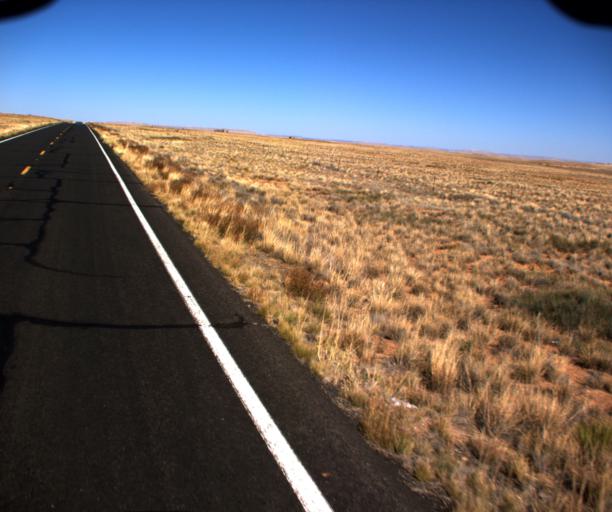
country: US
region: Arizona
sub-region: Navajo County
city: First Mesa
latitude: 35.6313
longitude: -110.4823
